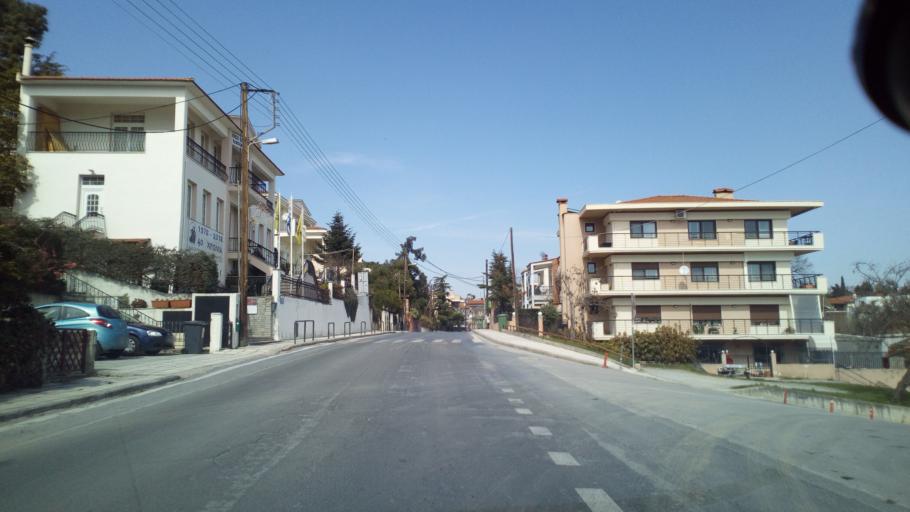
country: GR
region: Central Macedonia
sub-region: Nomos Thessalonikis
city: Panorama
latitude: 40.5869
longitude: 23.0353
